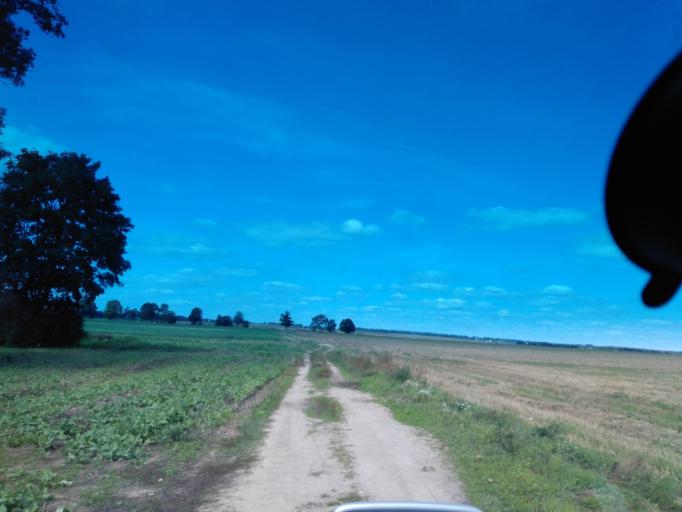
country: BY
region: Minsk
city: Stan'kava
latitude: 53.6303
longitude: 27.3272
